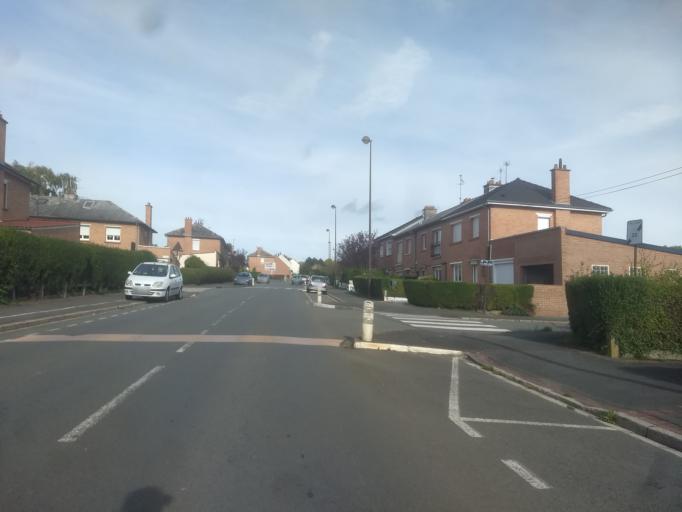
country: FR
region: Nord-Pas-de-Calais
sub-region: Departement du Pas-de-Calais
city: Dainville
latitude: 50.2894
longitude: 2.7426
